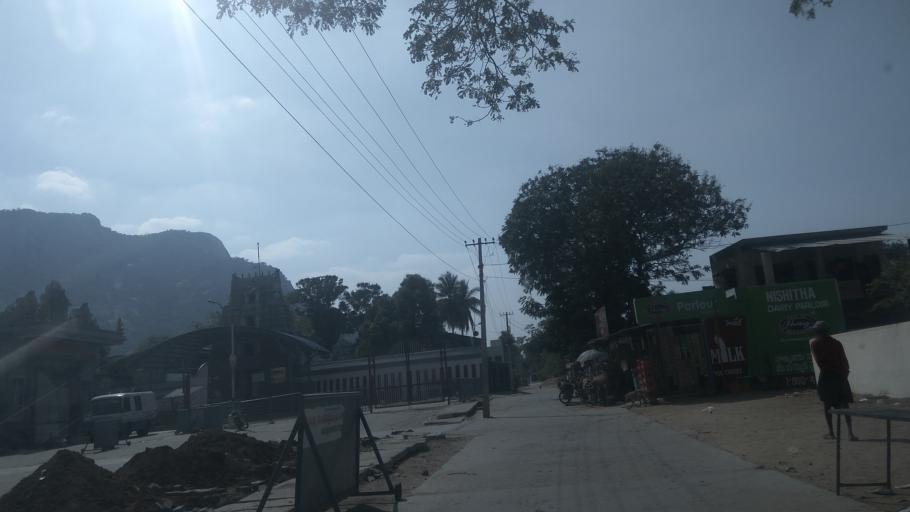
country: IN
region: Andhra Pradesh
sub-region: Chittoor
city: Renigunta
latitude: 13.5374
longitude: 79.4784
